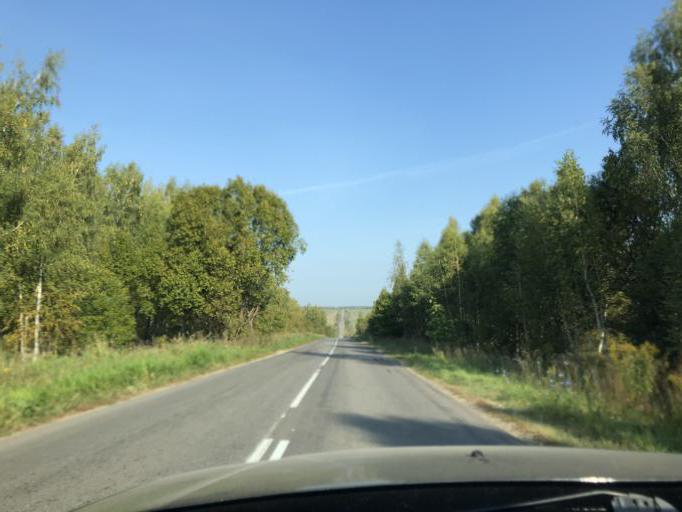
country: RU
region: Tula
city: Novogurovskiy
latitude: 54.3863
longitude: 37.3253
